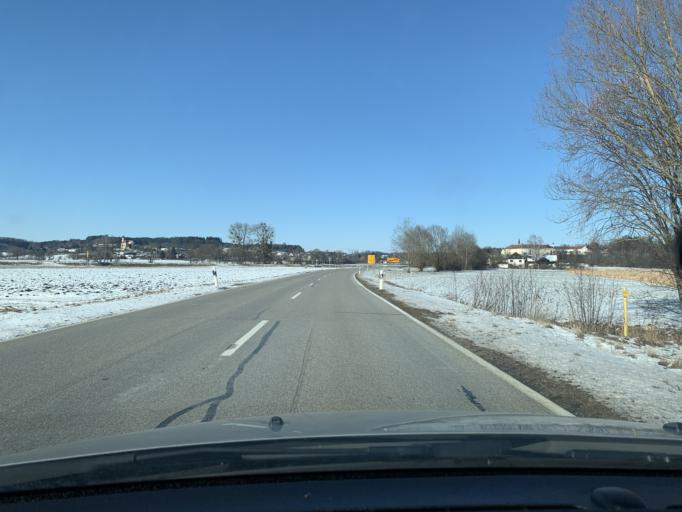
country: DE
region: Bavaria
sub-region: Upper Bavaria
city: Neufahrn
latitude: 48.2662
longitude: 12.4283
